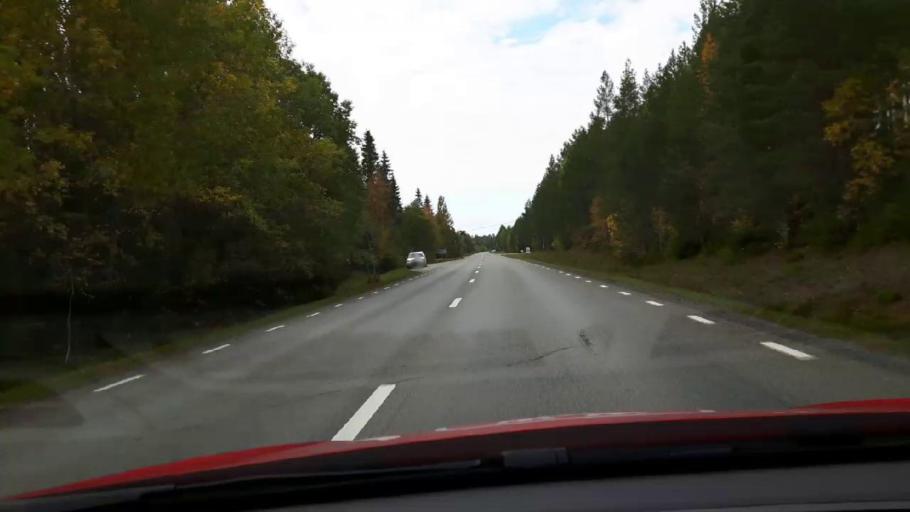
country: SE
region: Jaemtland
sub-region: Krokoms Kommun
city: Valla
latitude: 63.2569
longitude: 13.9898
